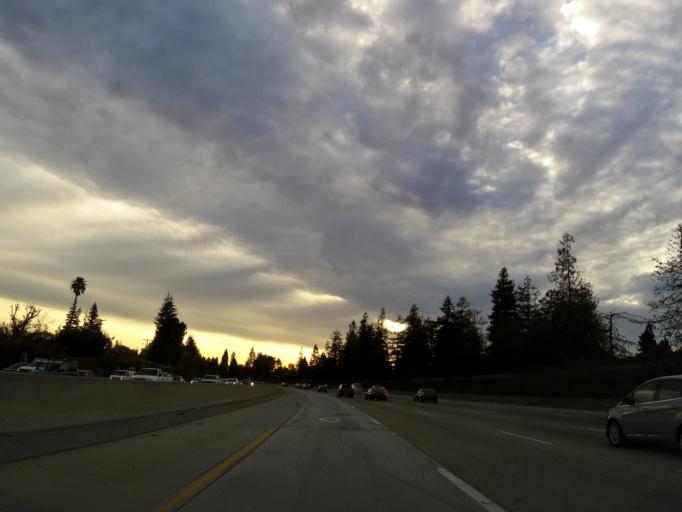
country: US
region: California
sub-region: Santa Clara County
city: Cupertino
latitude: 37.3187
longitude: -121.9915
